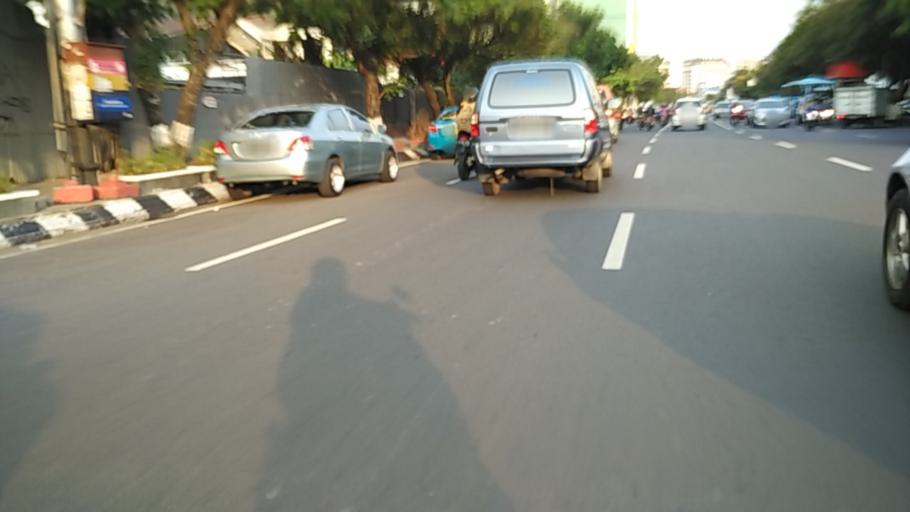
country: ID
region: Central Java
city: Semarang
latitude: -6.9867
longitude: 110.4148
